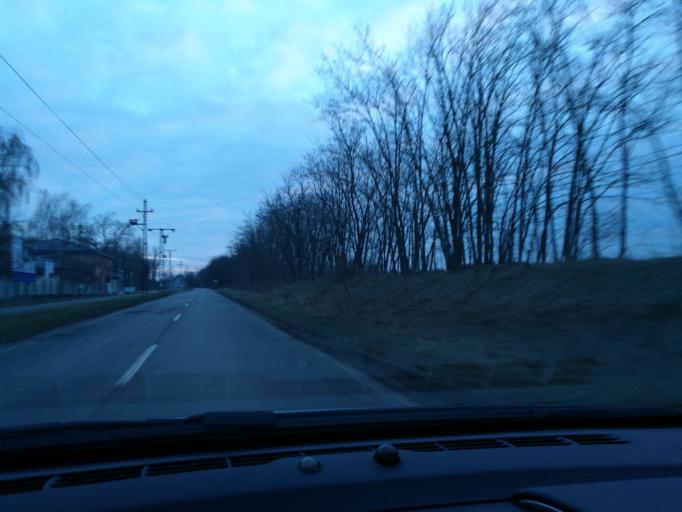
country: HU
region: Szabolcs-Szatmar-Bereg
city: Nyiregyhaza
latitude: 47.9808
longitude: 21.7048
